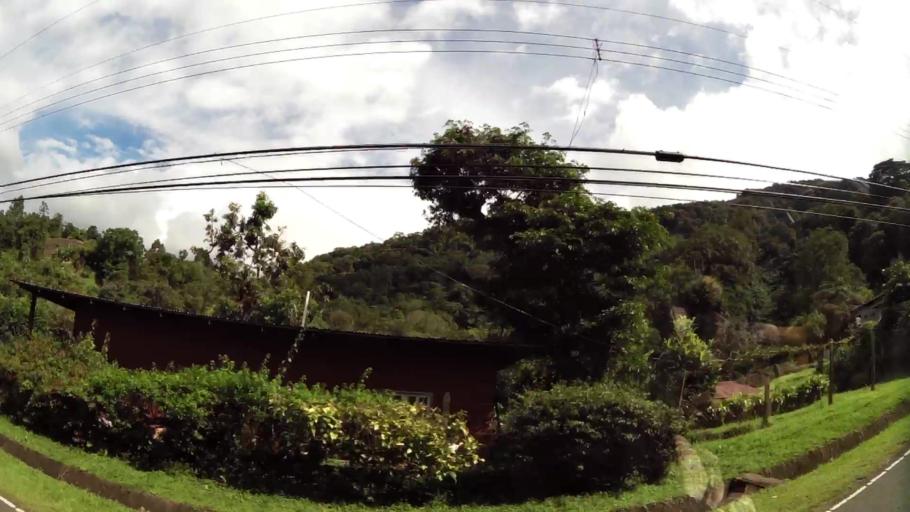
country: PA
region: Chiriqui
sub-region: Distrito Boquete
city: Boquete
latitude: 8.7884
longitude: -82.4239
